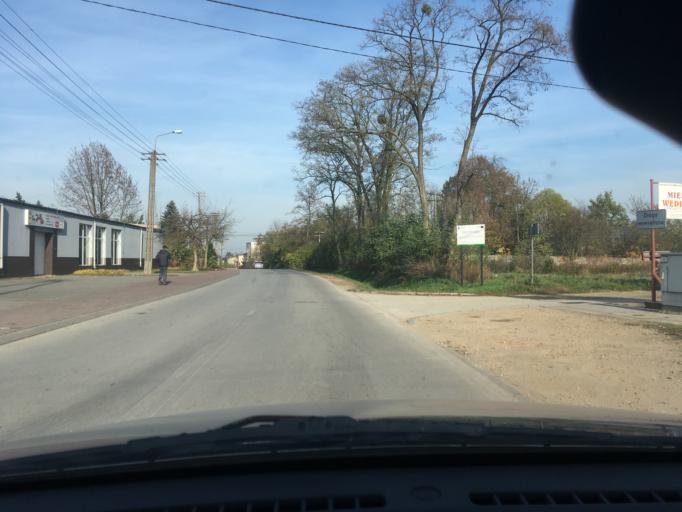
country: PL
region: Masovian Voivodeship
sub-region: Powiat plocki
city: Bodzanow
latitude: 52.4927
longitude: 20.0309
